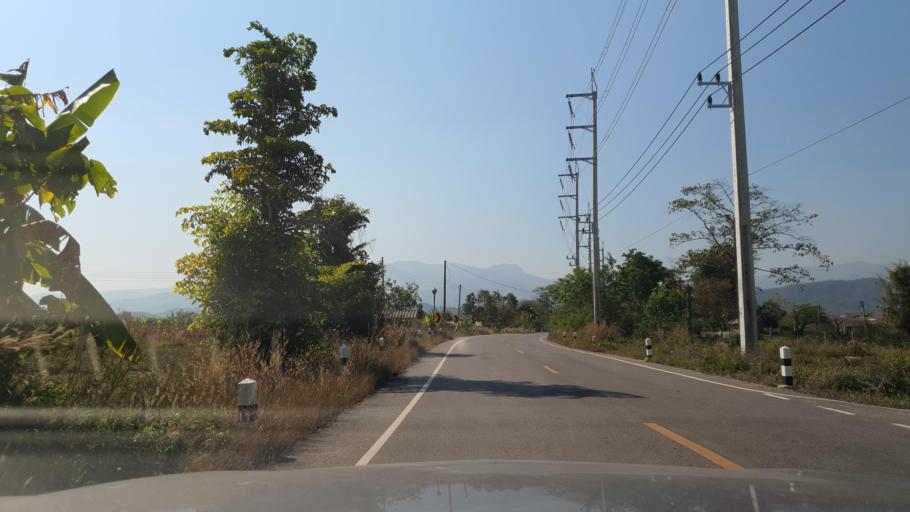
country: TH
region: Chiang Rai
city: Mae Lao
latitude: 19.8027
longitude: 99.6938
